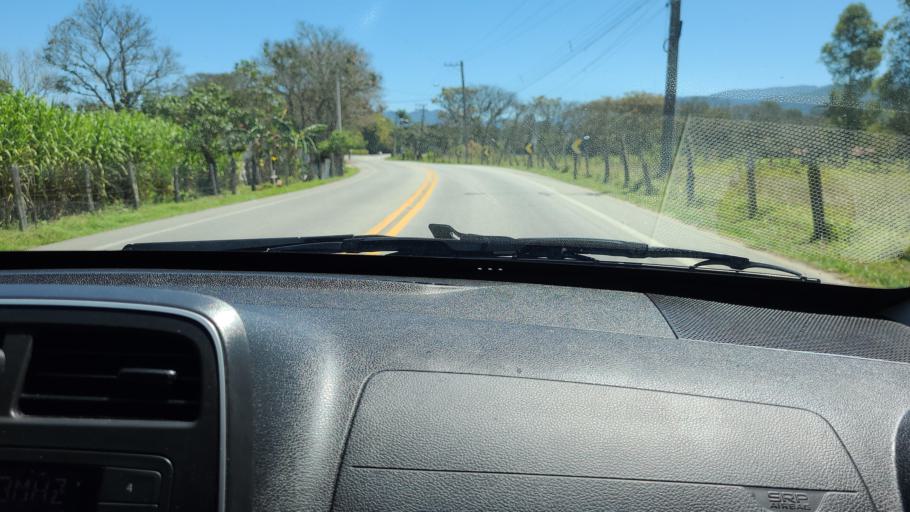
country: BR
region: Sao Paulo
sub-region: Pindamonhangaba
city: Pindamonhangaba
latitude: -22.8984
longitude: -45.4982
